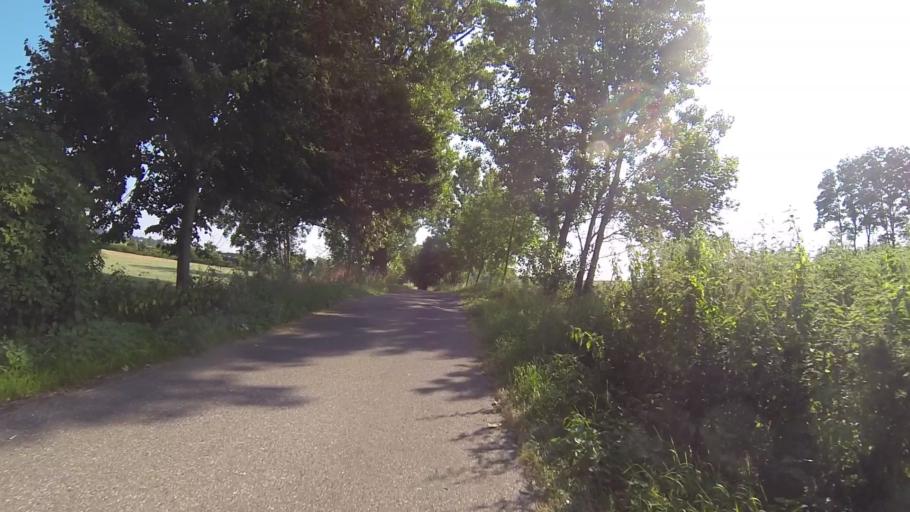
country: DE
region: Baden-Wuerttemberg
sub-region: Tuebingen Region
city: Erbach
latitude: 48.3453
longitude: 9.9150
